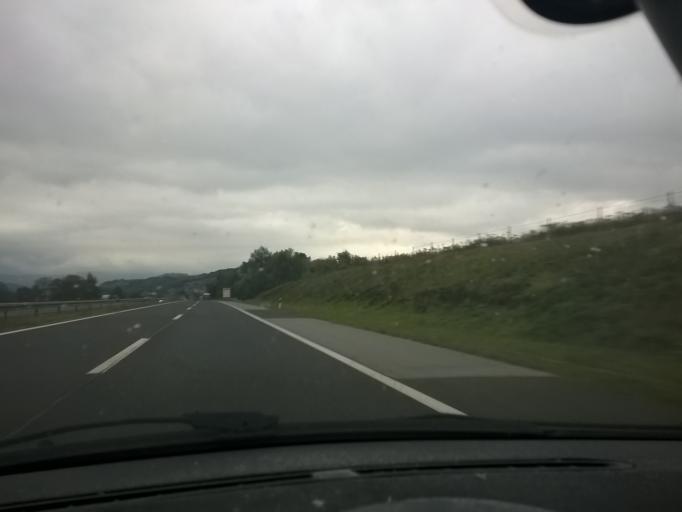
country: HR
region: Krapinsko-Zagorska
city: Zabok
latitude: 46.0614
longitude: 15.9196
